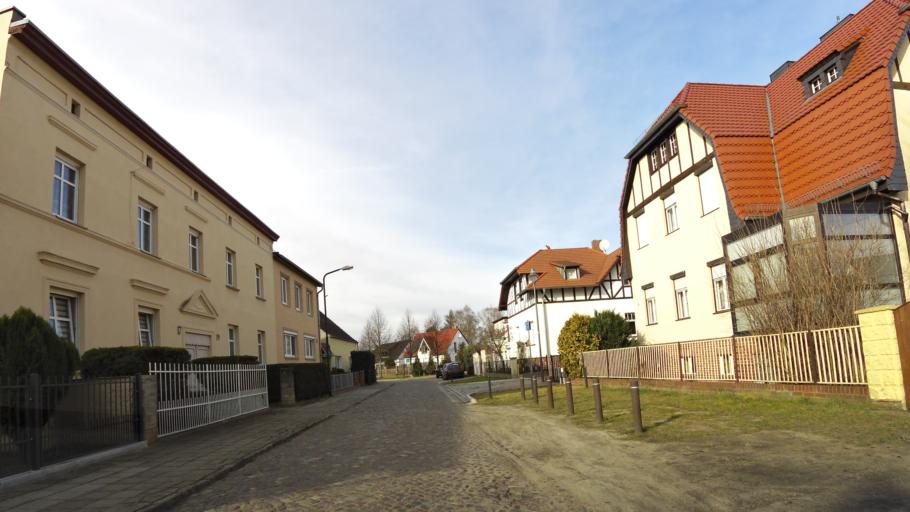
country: DE
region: Brandenburg
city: Michendorf
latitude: 52.3491
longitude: 12.9956
